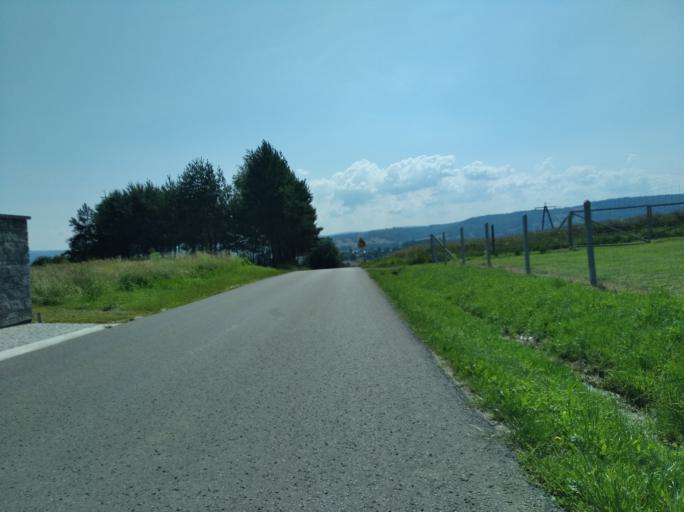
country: PL
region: Subcarpathian Voivodeship
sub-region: Powiat rzeszowski
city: Dynow
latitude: 49.8135
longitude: 22.2151
